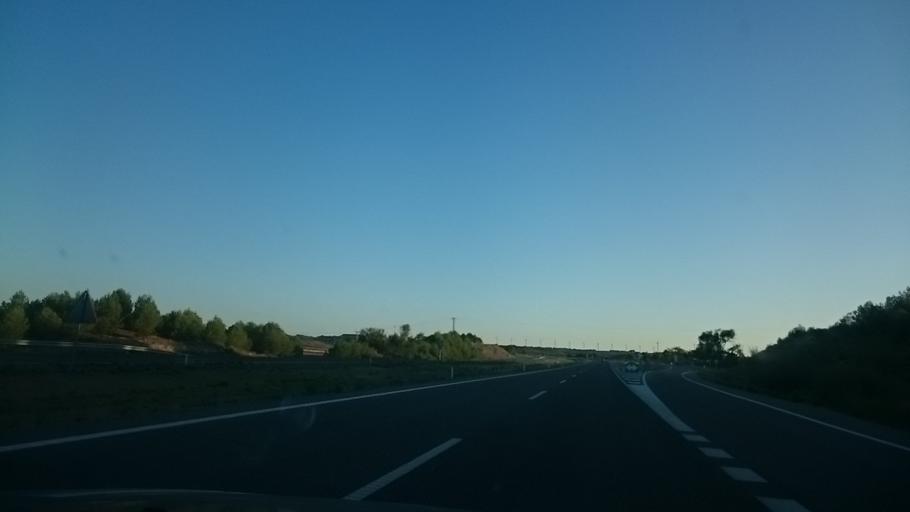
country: ES
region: Navarre
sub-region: Provincia de Navarra
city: Murchante
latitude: 42.0607
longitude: -1.6895
